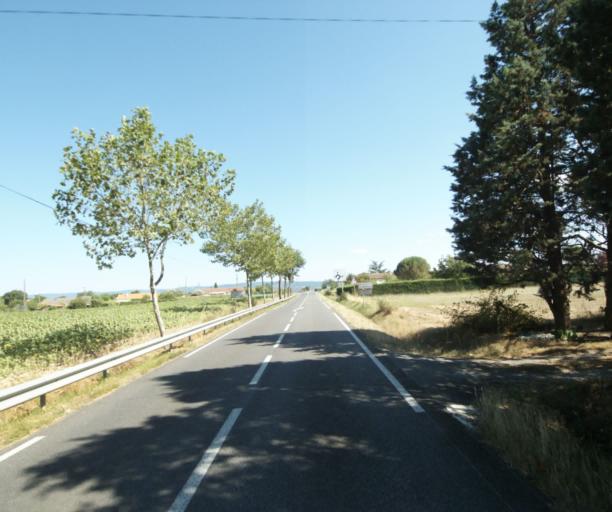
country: FR
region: Midi-Pyrenees
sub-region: Departement de la Haute-Garonne
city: Saint-Felix-Lauragais
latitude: 43.4823
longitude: 1.9147
